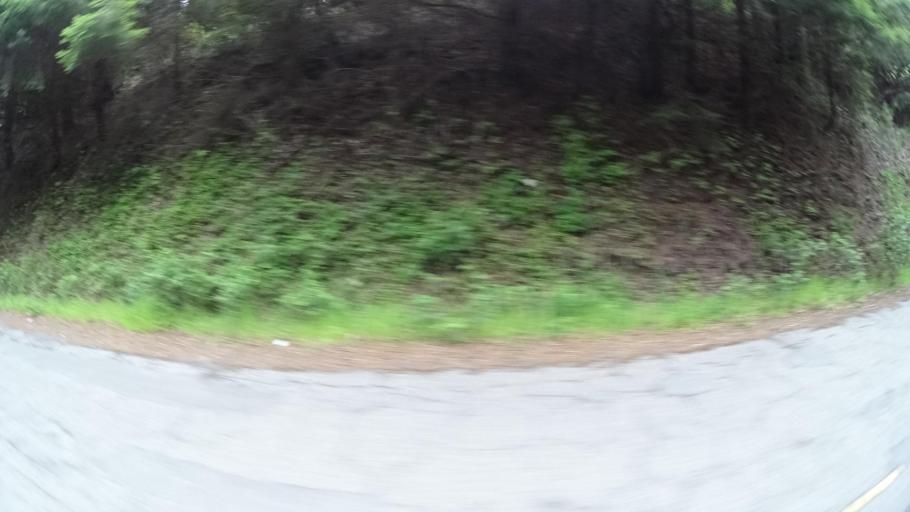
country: US
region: California
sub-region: Humboldt County
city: Blue Lake
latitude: 40.8730
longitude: -123.9740
